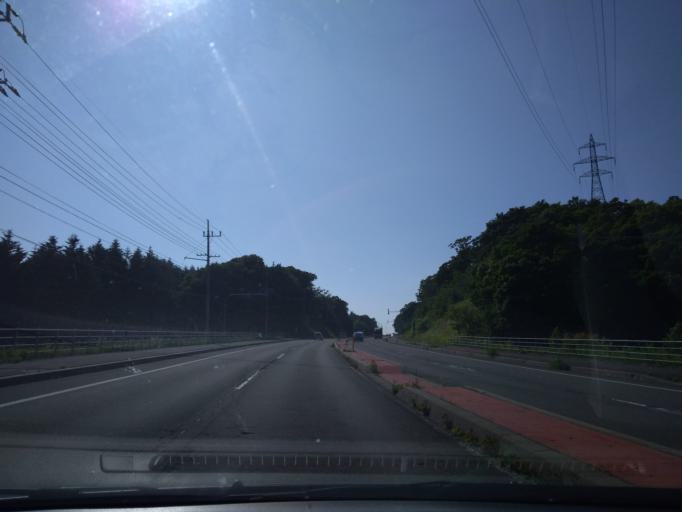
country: JP
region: Hokkaido
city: Kitahiroshima
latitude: 42.9778
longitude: 141.5098
